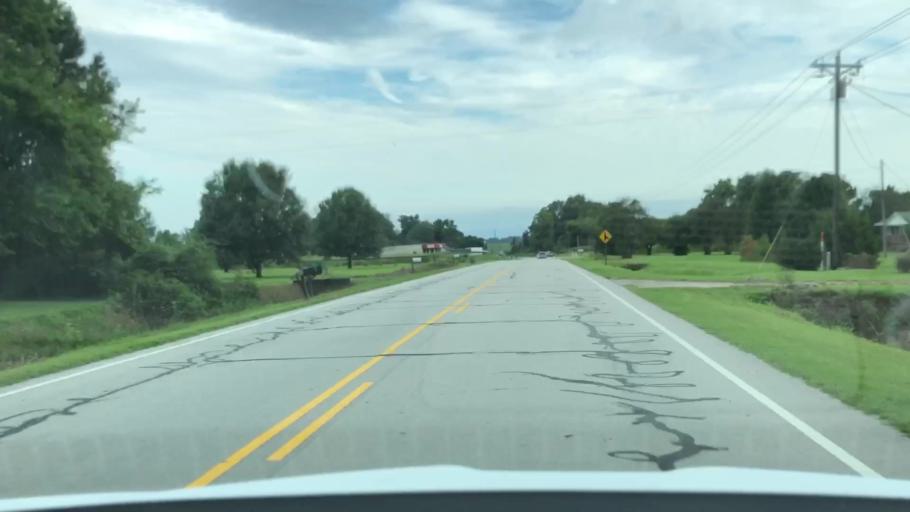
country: US
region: North Carolina
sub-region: Lenoir County
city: Kinston
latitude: 35.1359
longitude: -77.5278
